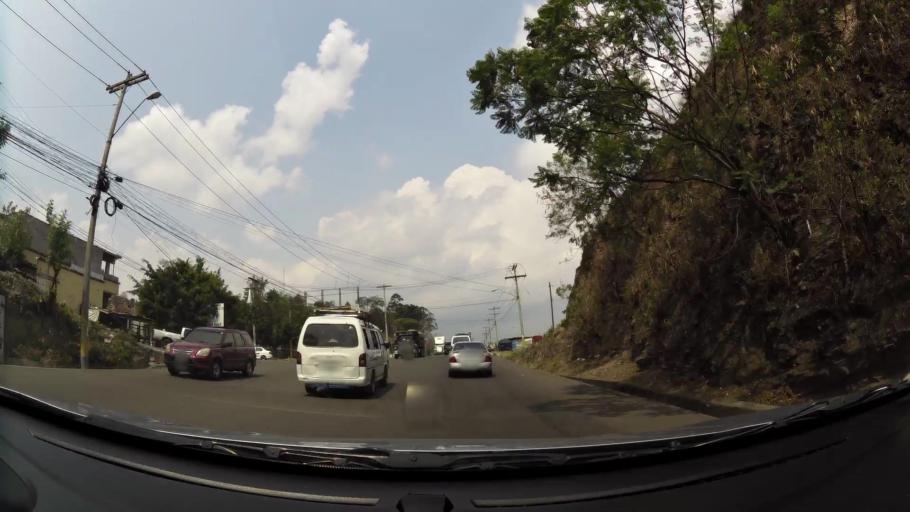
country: HN
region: Francisco Morazan
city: Tegucigalpa
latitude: 14.1137
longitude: -87.2271
